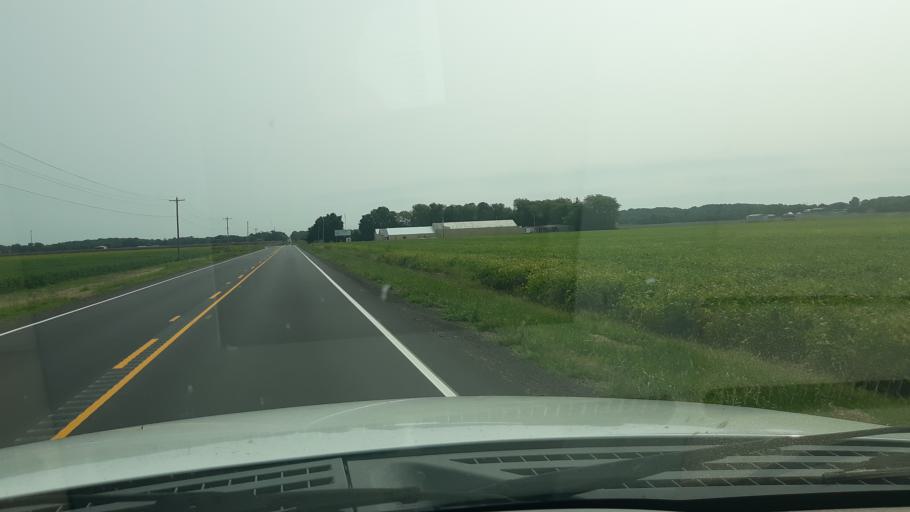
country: US
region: Indiana
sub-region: Gibson County
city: Princeton
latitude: 38.3557
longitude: -87.6488
